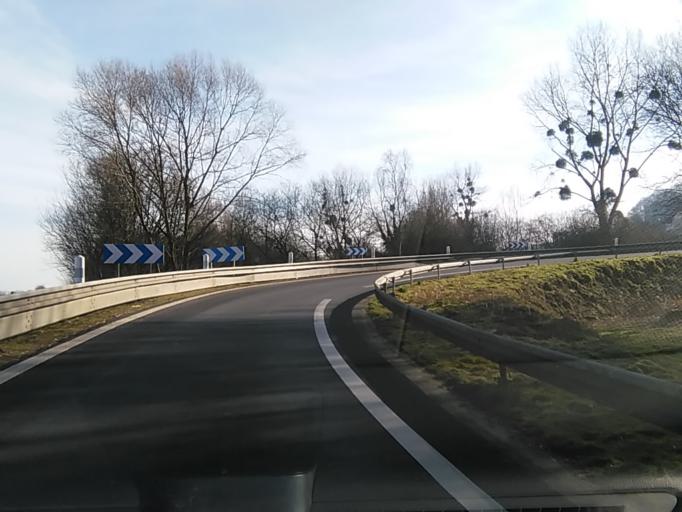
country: FR
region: Lower Normandy
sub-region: Departement de la Manche
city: Avranches
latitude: 48.6909
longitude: -1.3629
